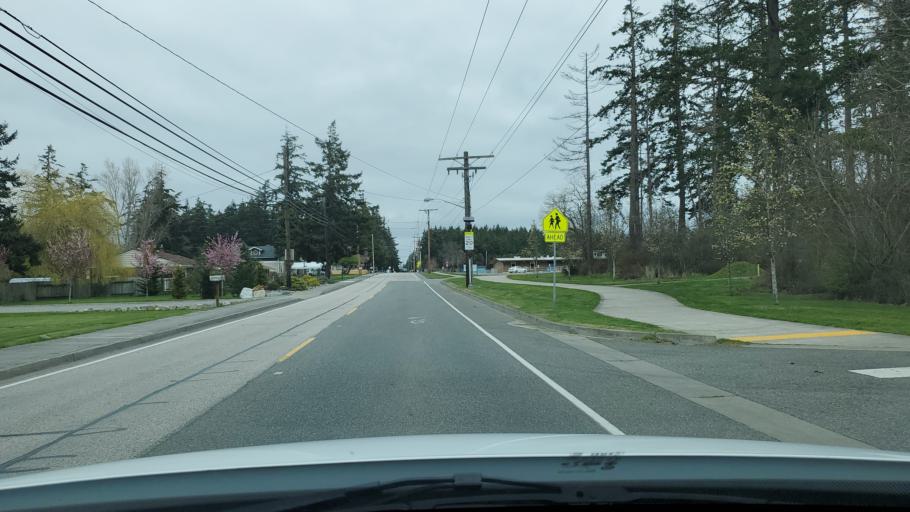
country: US
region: Washington
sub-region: Island County
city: Oak Harbor
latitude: 48.2997
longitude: -122.6349
